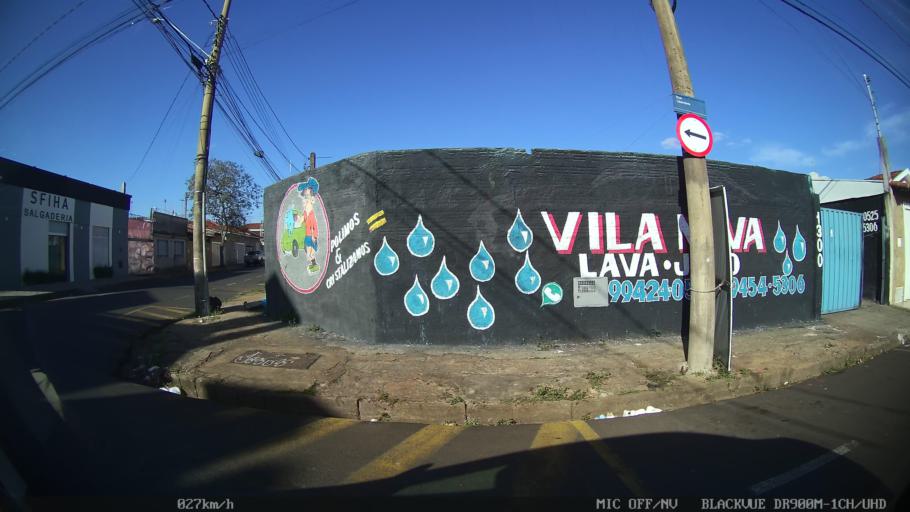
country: BR
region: Sao Paulo
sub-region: Franca
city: Franca
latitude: -20.5301
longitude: -47.4181
